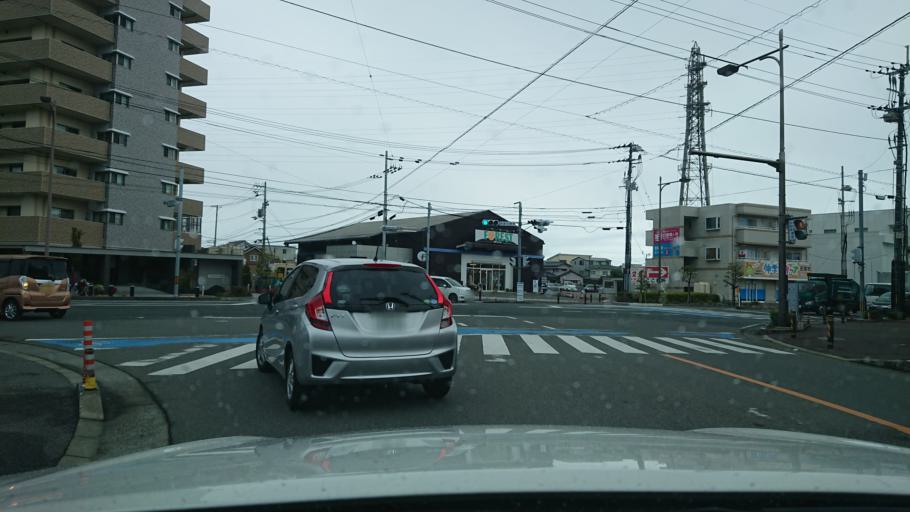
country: JP
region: Tokushima
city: Tokushima-shi
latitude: 34.0864
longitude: 134.5393
